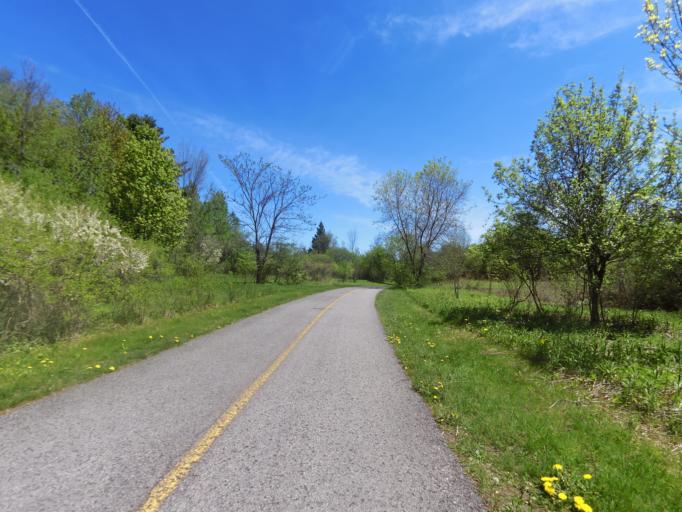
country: CA
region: Ontario
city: Ottawa
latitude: 45.4310
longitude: -75.7707
